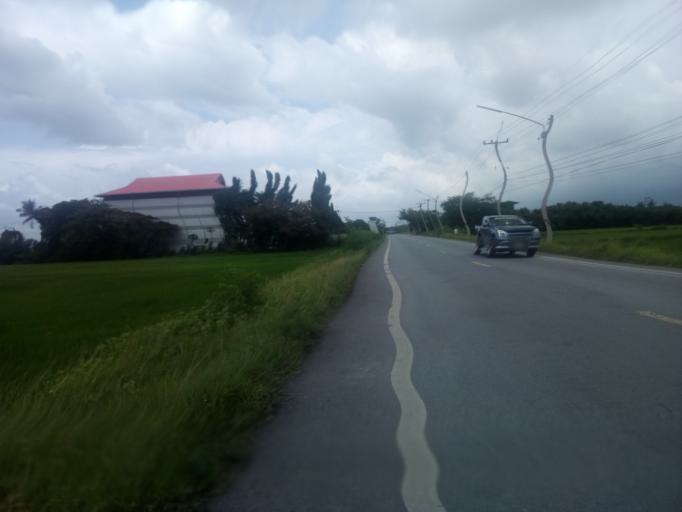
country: TH
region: Pathum Thani
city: Ban Lam Luk Ka
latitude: 13.9901
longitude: 100.8212
